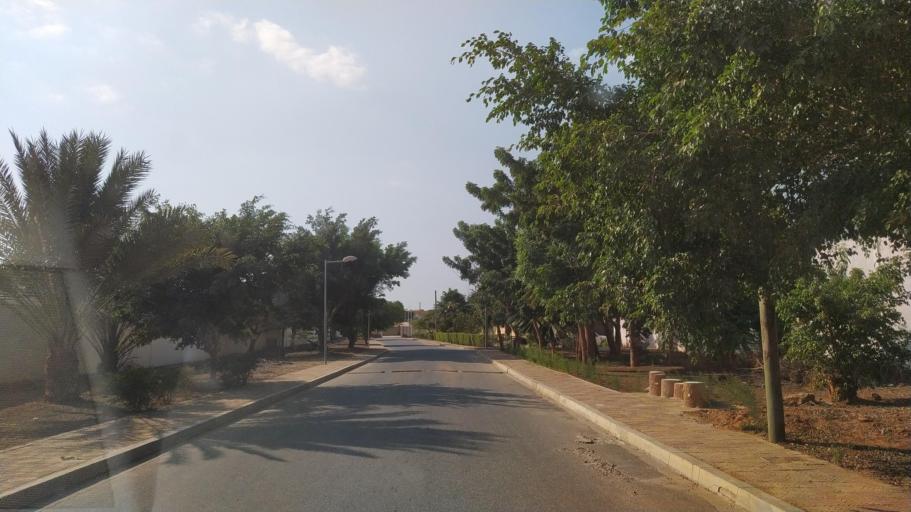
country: AO
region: Luanda
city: Luanda
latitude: -8.8928
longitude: 13.2572
